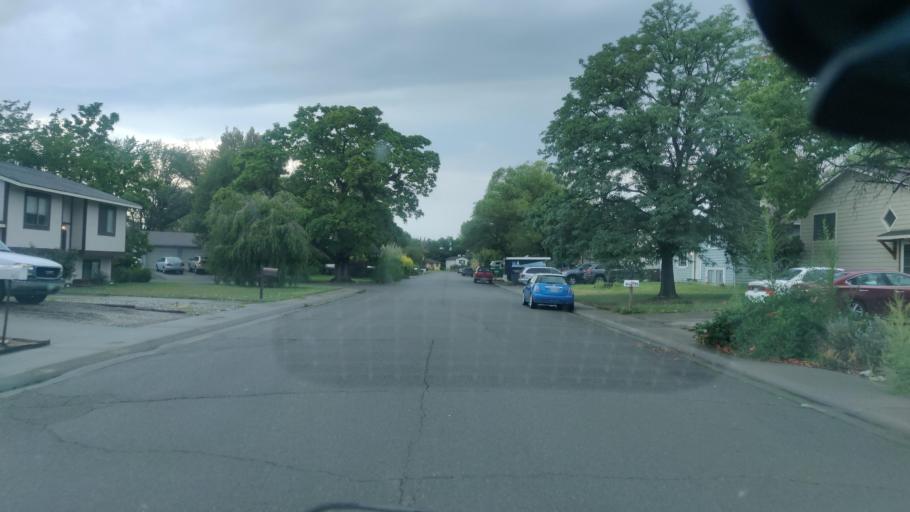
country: US
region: Colorado
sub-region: Mesa County
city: Fruitvale
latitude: 39.0853
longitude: -108.4979
